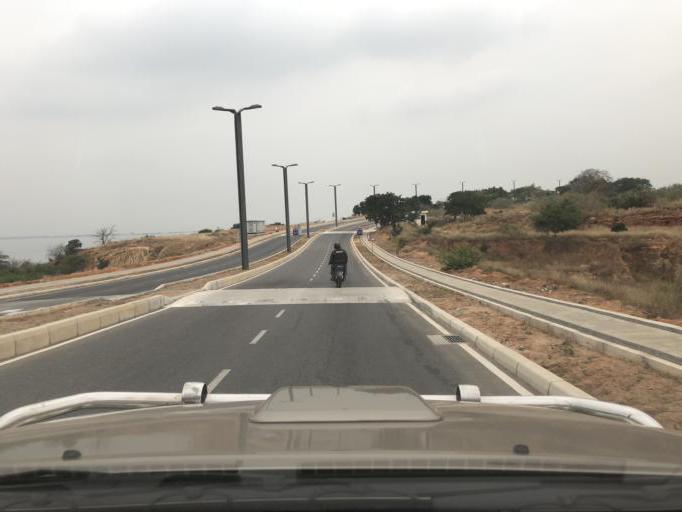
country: AO
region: Luanda
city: Luanda
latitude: -8.8959
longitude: 13.1753
